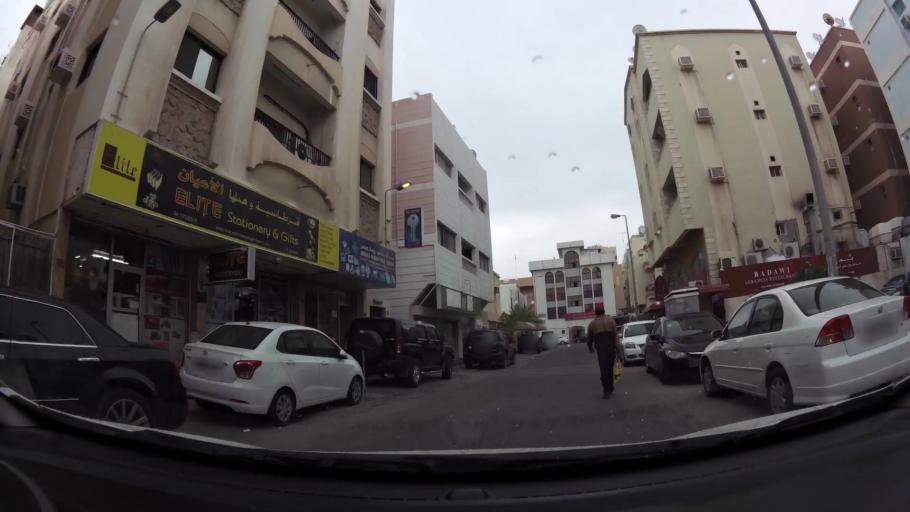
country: BH
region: Manama
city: Manama
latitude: 26.2347
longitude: 50.5923
